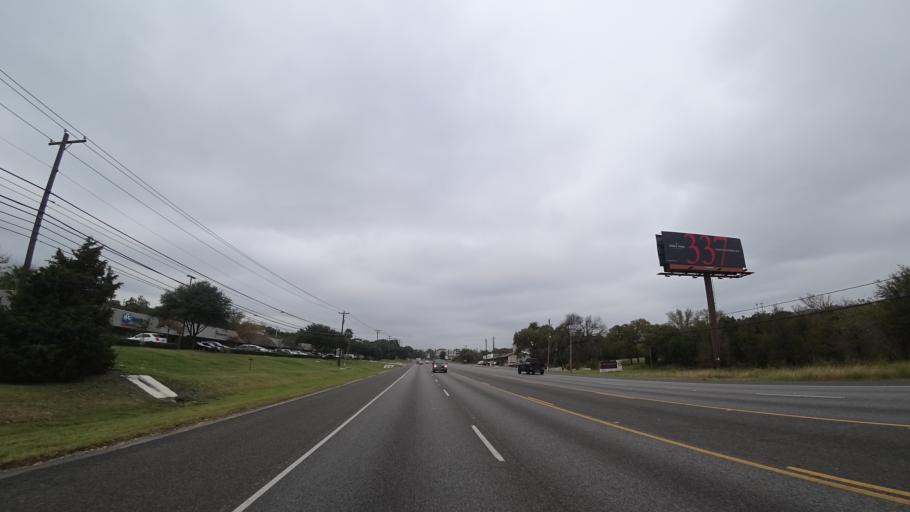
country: US
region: Texas
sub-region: Travis County
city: Barton Creek
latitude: 30.2380
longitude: -97.8790
